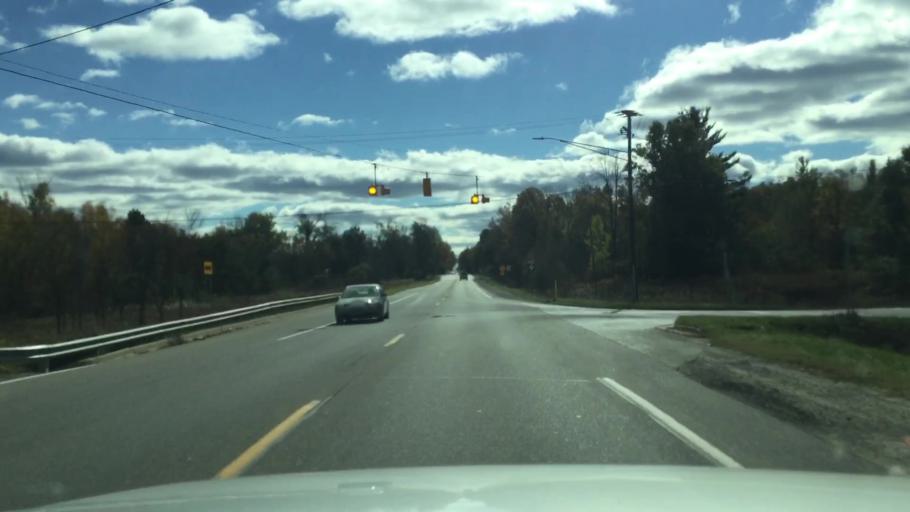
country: US
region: Michigan
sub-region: Lapeer County
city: Barnes Lake-Millers Lake
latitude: 43.1612
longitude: -83.3117
